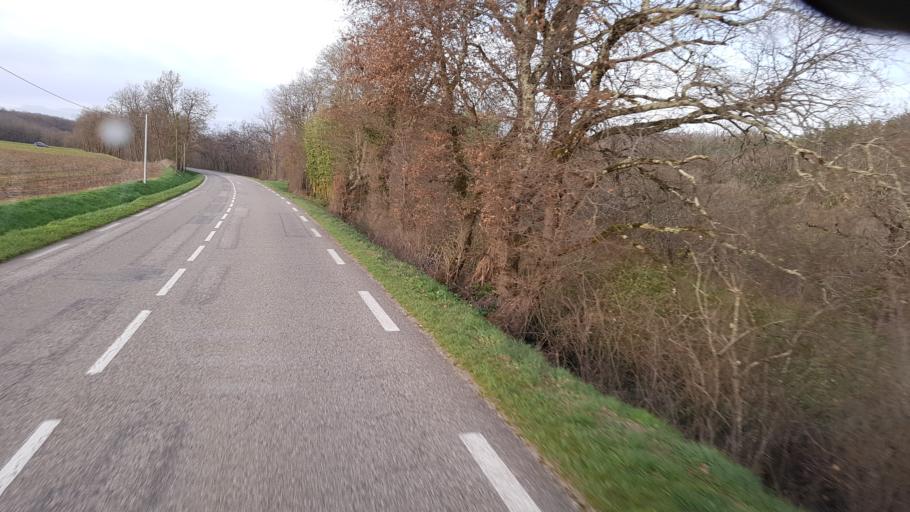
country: FR
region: Midi-Pyrenees
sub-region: Departement du Tarn-et-Garonne
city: Montricoux
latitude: 44.0732
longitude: 1.6397
